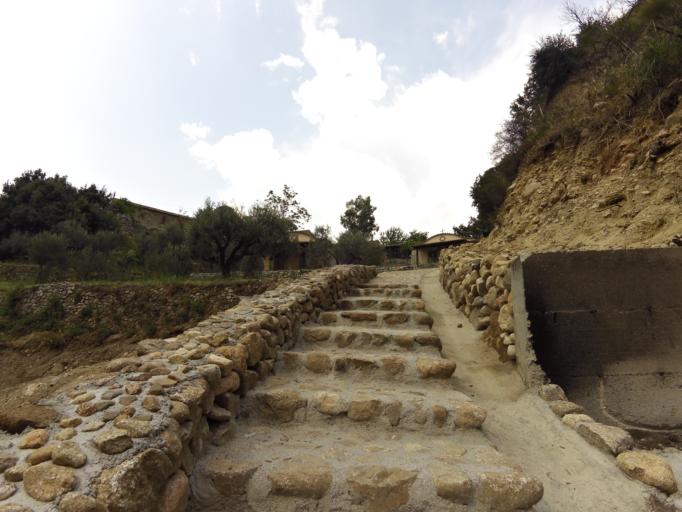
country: IT
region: Calabria
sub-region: Provincia di Reggio Calabria
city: Stilo
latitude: 38.4943
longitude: 16.4710
